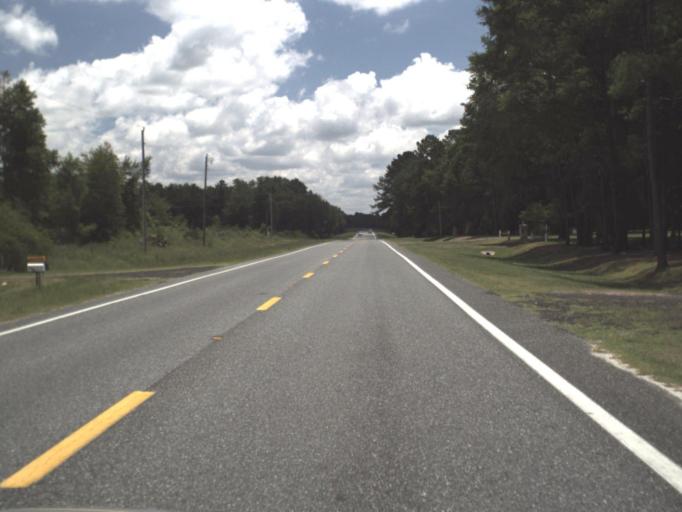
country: US
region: Florida
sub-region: Suwannee County
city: Wellborn
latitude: 30.3202
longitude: -82.7935
